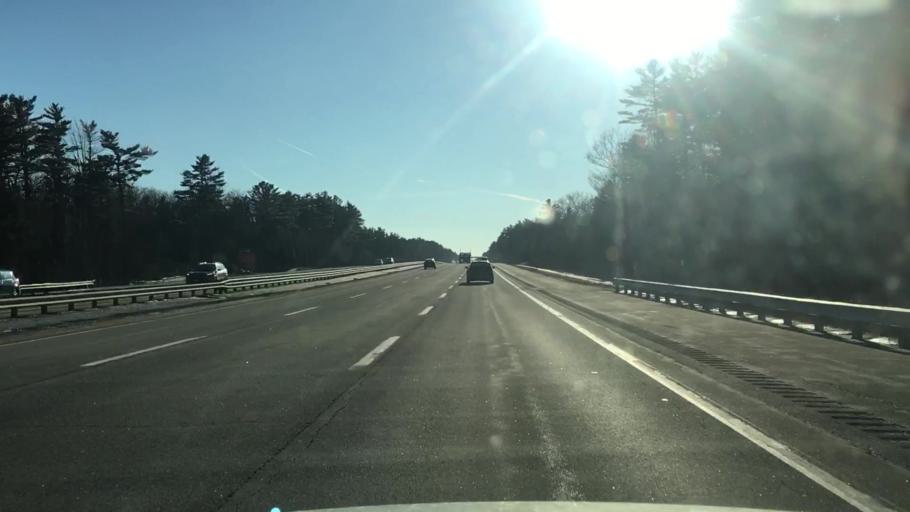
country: US
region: Maine
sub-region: Cumberland County
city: West Scarborough
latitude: 43.5690
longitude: -70.4094
